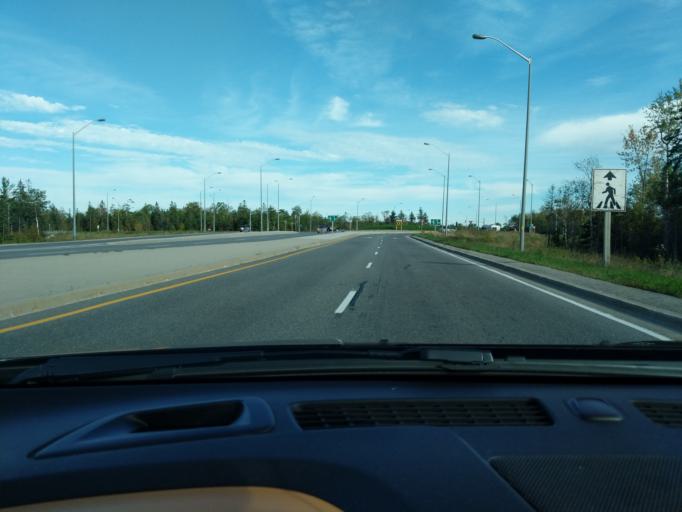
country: CA
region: Ontario
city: Collingwood
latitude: 44.4621
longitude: -80.1149
